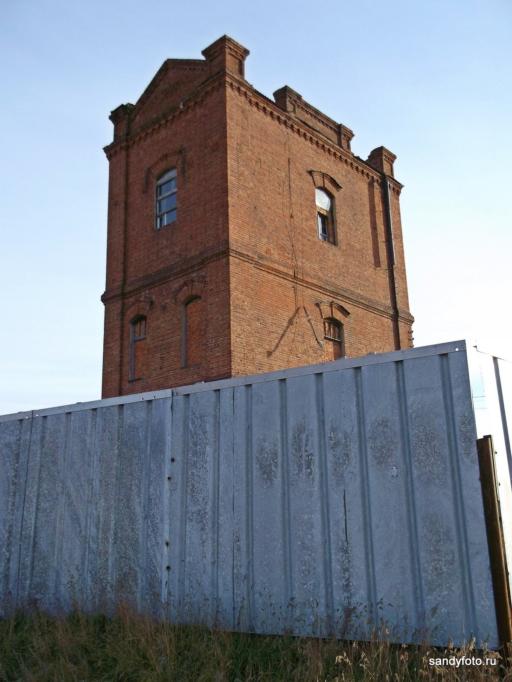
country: RU
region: Chelyabinsk
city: Troitsk
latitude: 54.0786
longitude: 61.5883
